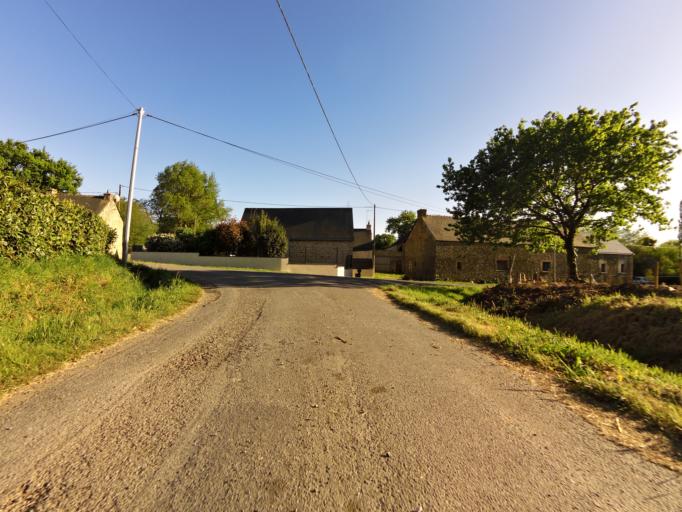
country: FR
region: Brittany
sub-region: Departement du Morbihan
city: Pluherlin
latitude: 47.7237
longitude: -2.3559
